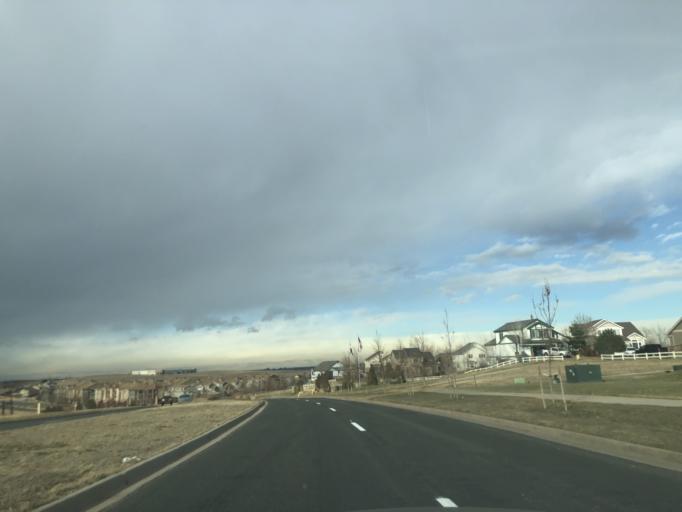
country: US
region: Colorado
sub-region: Douglas County
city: Stonegate
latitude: 39.5581
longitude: -104.8068
